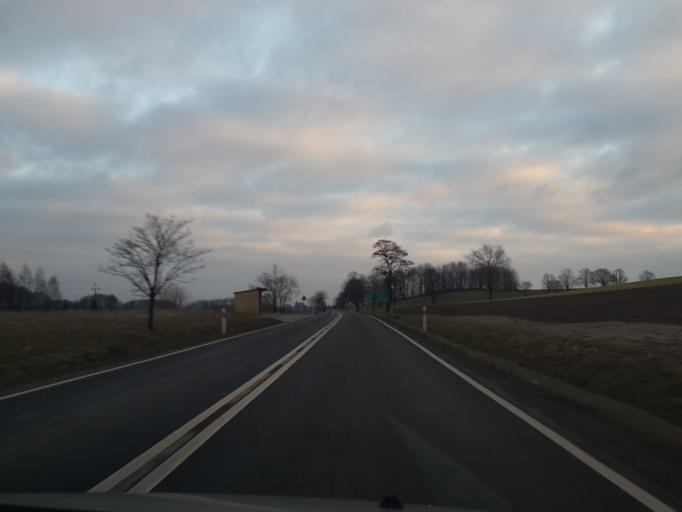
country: PL
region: Warmian-Masurian Voivodeship
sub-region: Powiat ilawski
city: Lubawa
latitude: 53.5625
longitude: 19.7770
